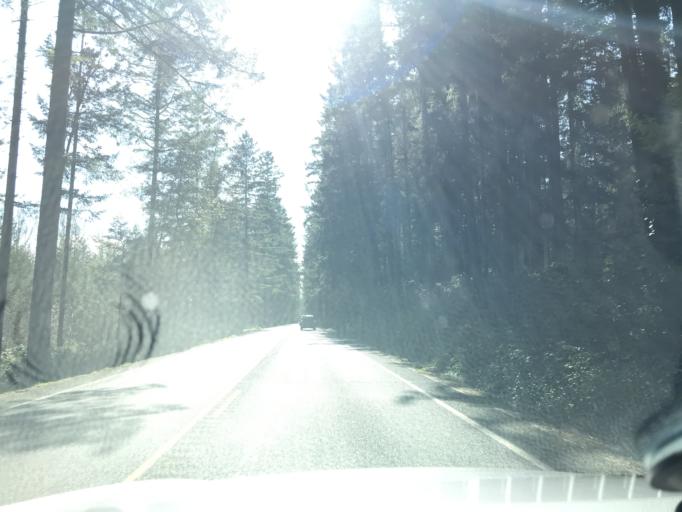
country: US
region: Washington
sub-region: Pierce County
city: Key Center
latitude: 47.3552
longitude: -122.7334
